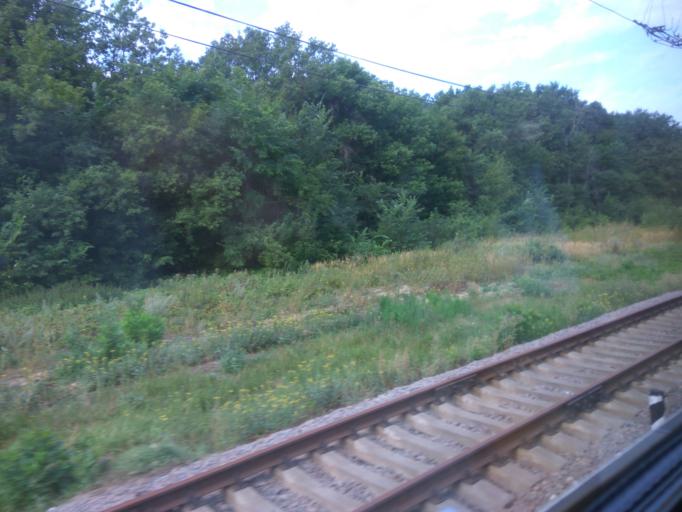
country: RU
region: Saratov
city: Rtishchevo
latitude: 52.2039
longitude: 43.8923
